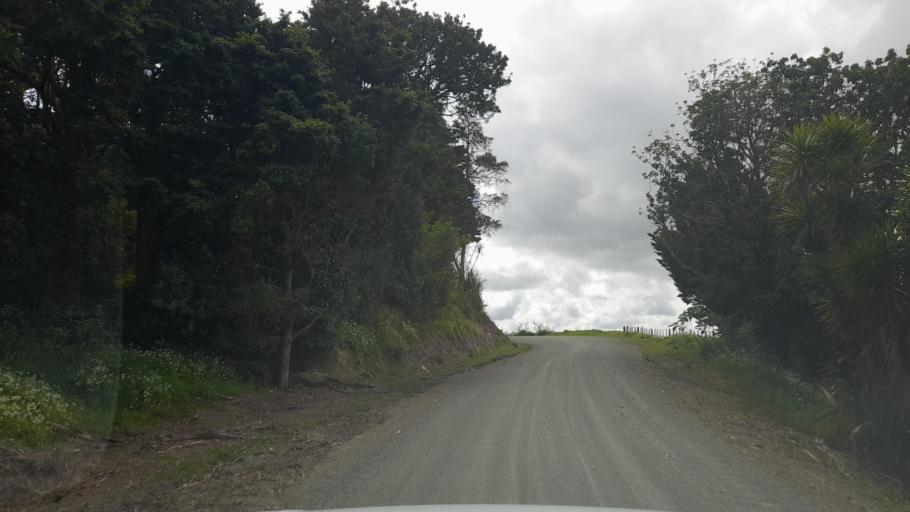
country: NZ
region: Auckland
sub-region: Auckland
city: Wellsford
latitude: -36.1771
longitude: 174.3491
